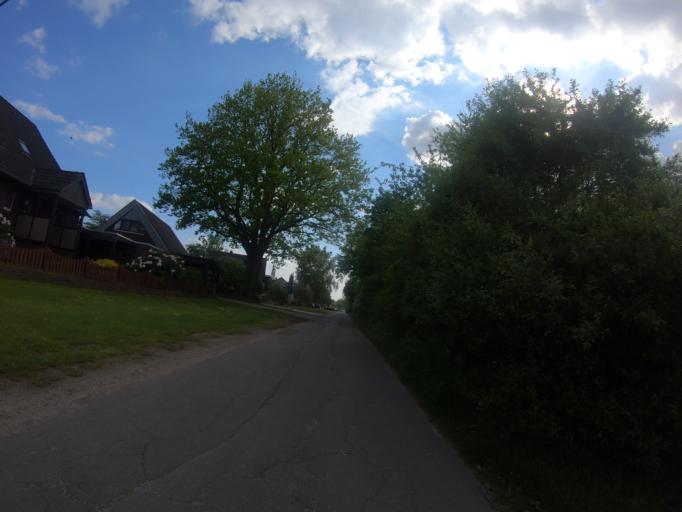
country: DE
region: Lower Saxony
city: Sassenburg
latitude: 52.5086
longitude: 10.6192
